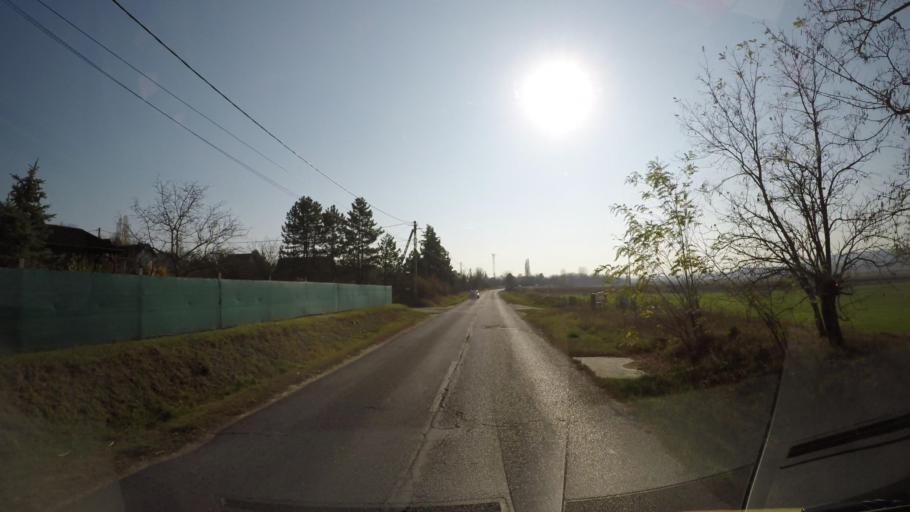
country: HU
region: Pest
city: Leanyfalu
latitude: 47.7062
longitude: 19.1073
